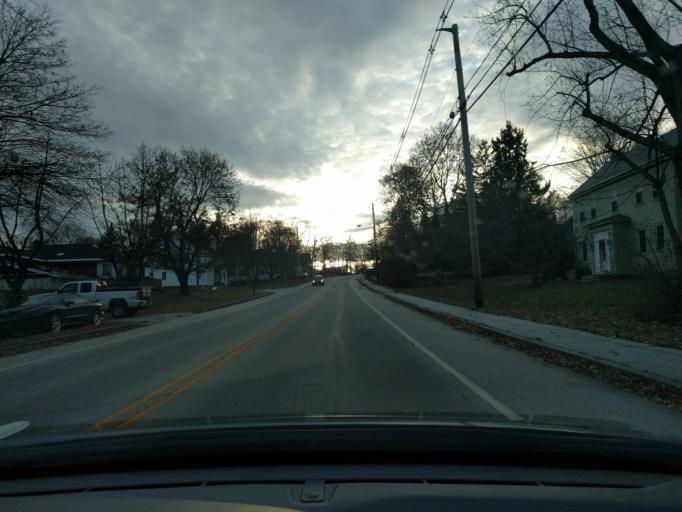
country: US
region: Maine
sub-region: Waldo County
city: Winterport
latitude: 44.6320
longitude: -68.8519
